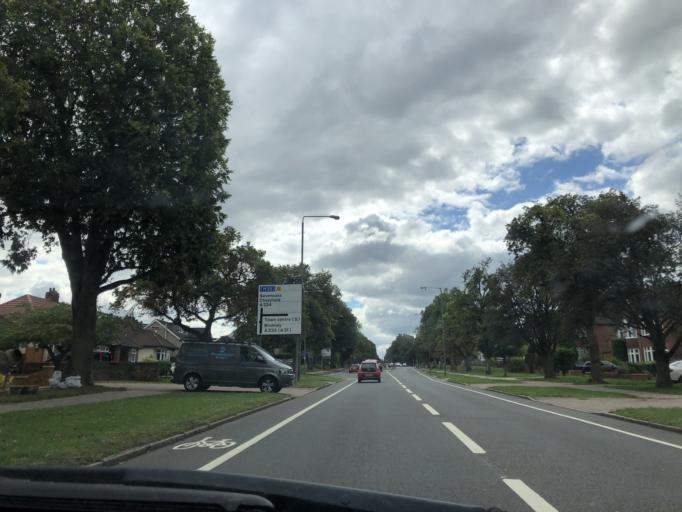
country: GB
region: England
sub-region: Greater London
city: Orpington
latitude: 51.3739
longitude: 0.1092
